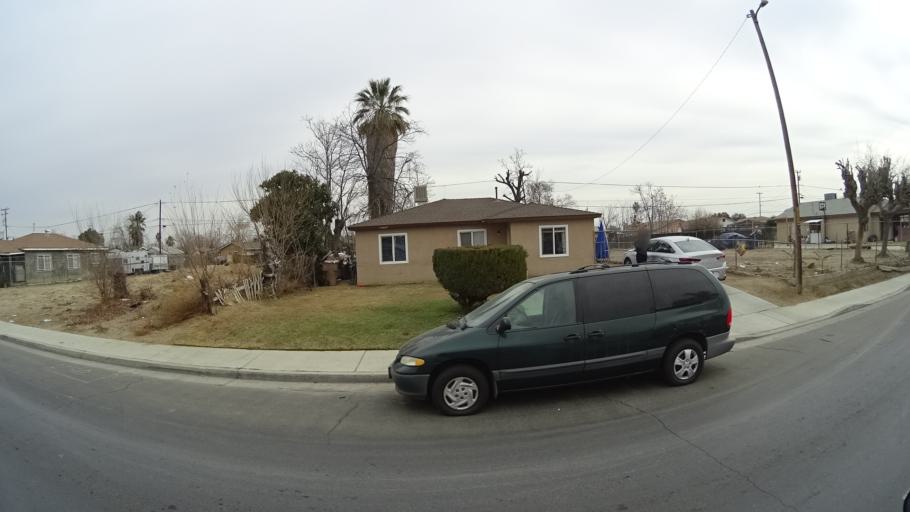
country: US
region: California
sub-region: Kern County
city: Bakersfield
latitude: 35.3602
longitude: -118.9908
